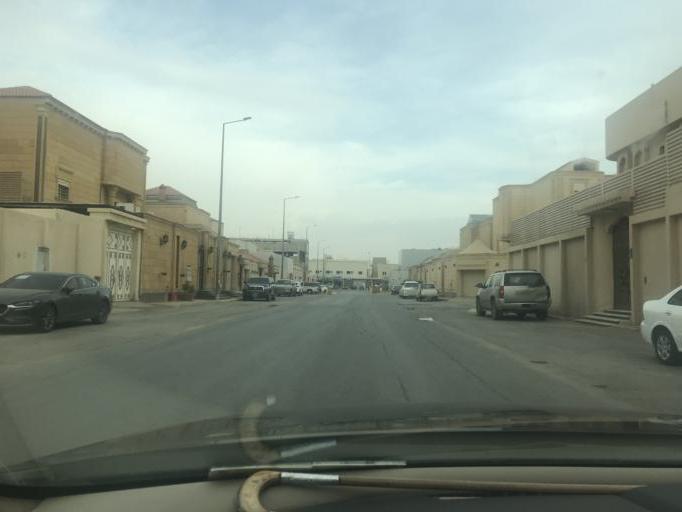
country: SA
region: Ar Riyad
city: Riyadh
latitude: 24.7491
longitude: 46.7719
